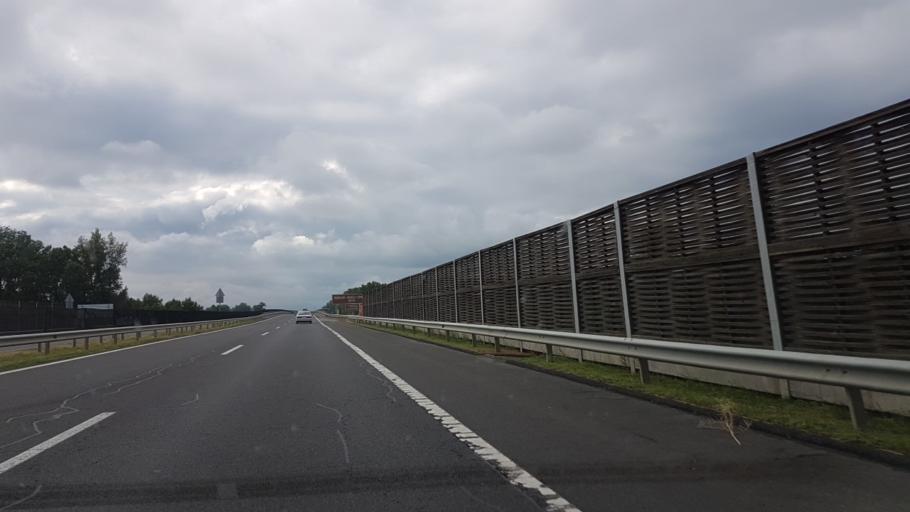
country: HU
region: Hajdu-Bihar
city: Polgar
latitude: 47.8538
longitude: 21.0575
